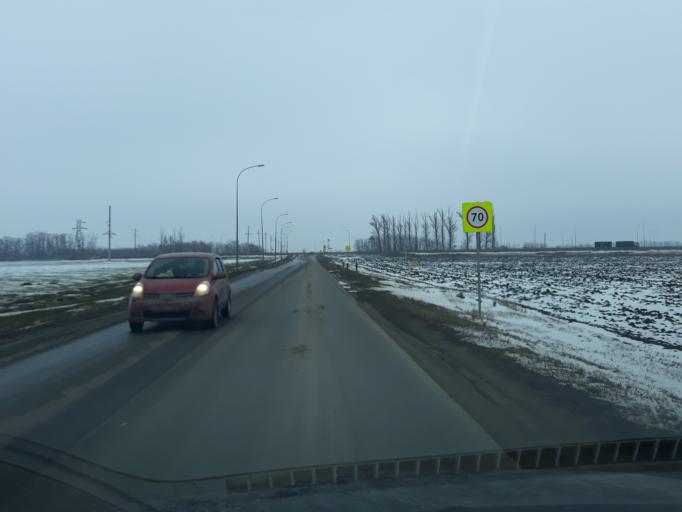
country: RU
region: Rostov
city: Severnyy
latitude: 47.3668
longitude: 39.6403
